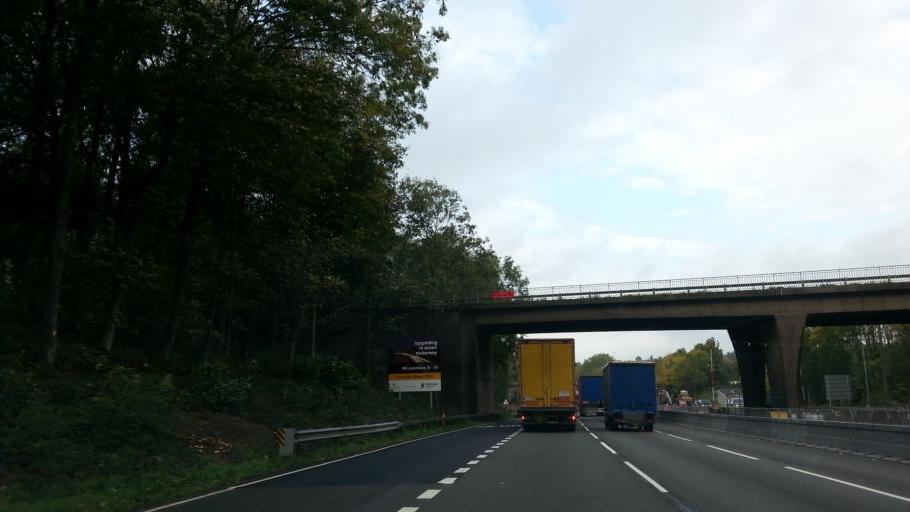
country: GB
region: England
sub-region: Staffordshire
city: Newcastle under Lyme
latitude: 52.9731
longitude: -2.2265
